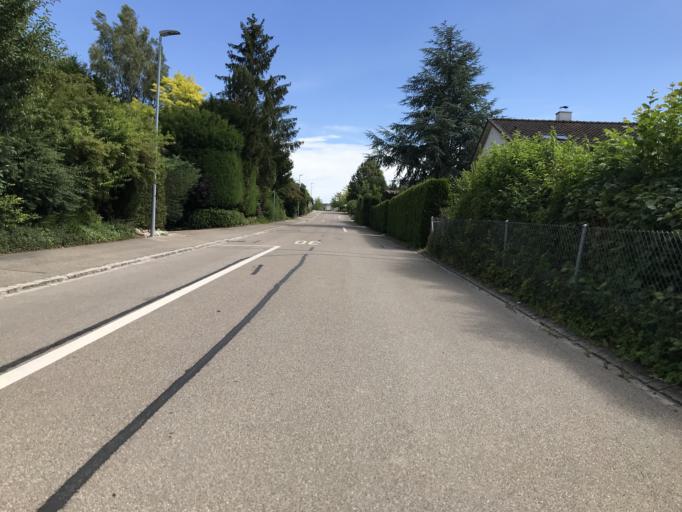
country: CH
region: Zurich
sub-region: Bezirk Winterthur
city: Neftenbach / Dorf Neftenbach
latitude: 47.5218
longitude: 8.6716
